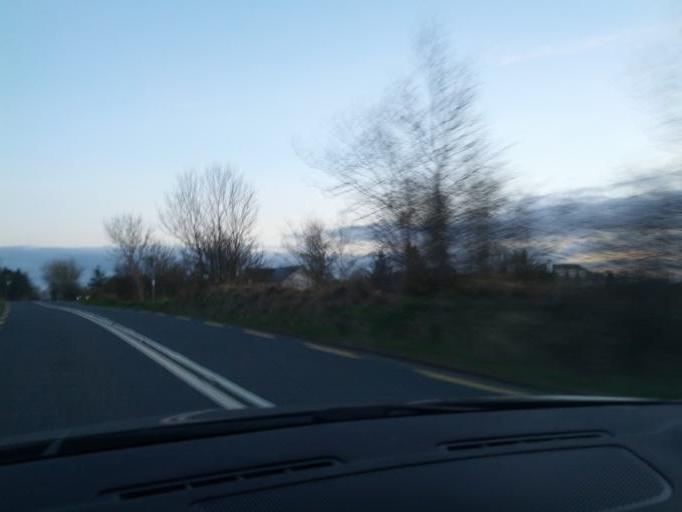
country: IE
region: Connaught
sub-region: Roscommon
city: Boyle
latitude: 53.9333
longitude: -8.2774
